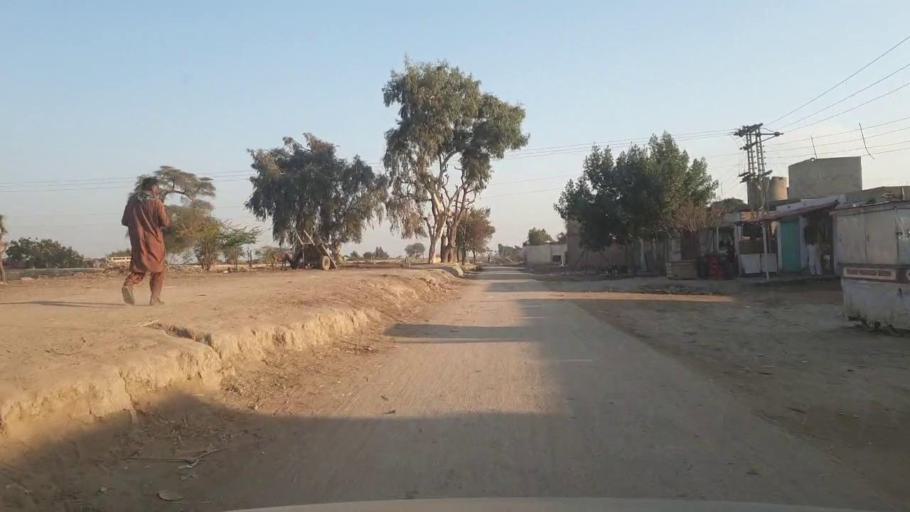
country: PK
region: Sindh
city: Chambar
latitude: 25.2939
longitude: 68.8930
